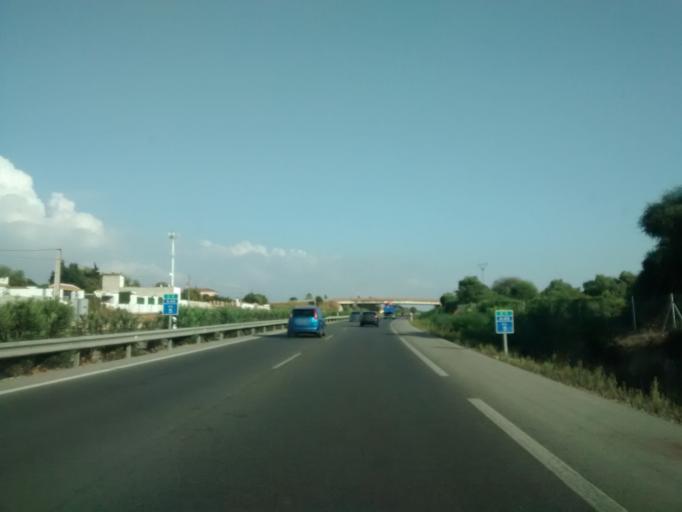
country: ES
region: Andalusia
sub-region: Provincia de Cadiz
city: Chiclana de la Frontera
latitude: 36.4388
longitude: -6.1261
